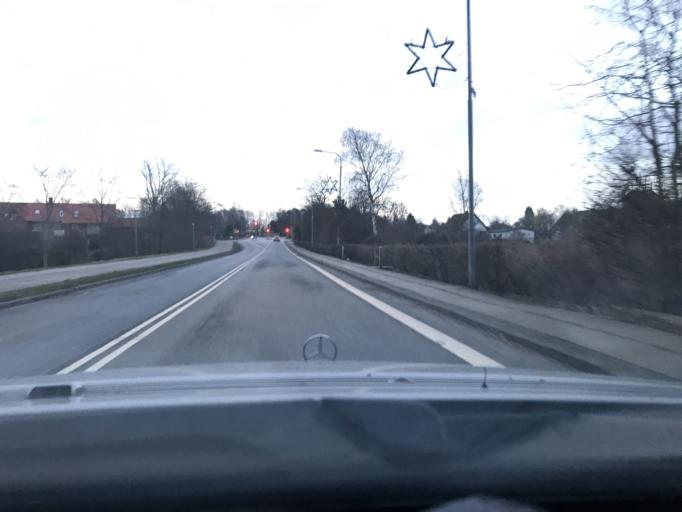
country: DK
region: South Denmark
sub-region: Sonderborg Kommune
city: Nordborg
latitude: 55.0548
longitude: 9.7459
